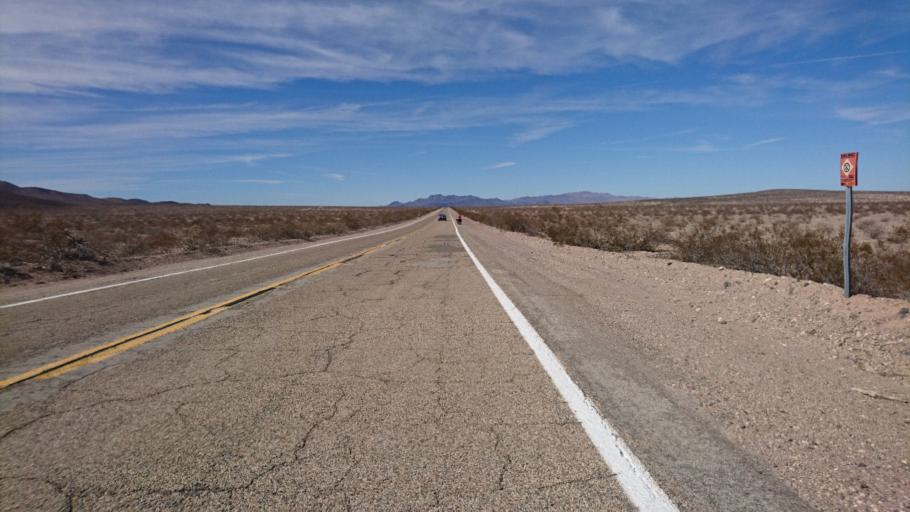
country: US
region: California
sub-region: San Bernardino County
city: Twentynine Palms
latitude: 34.7028
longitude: -116.0701
